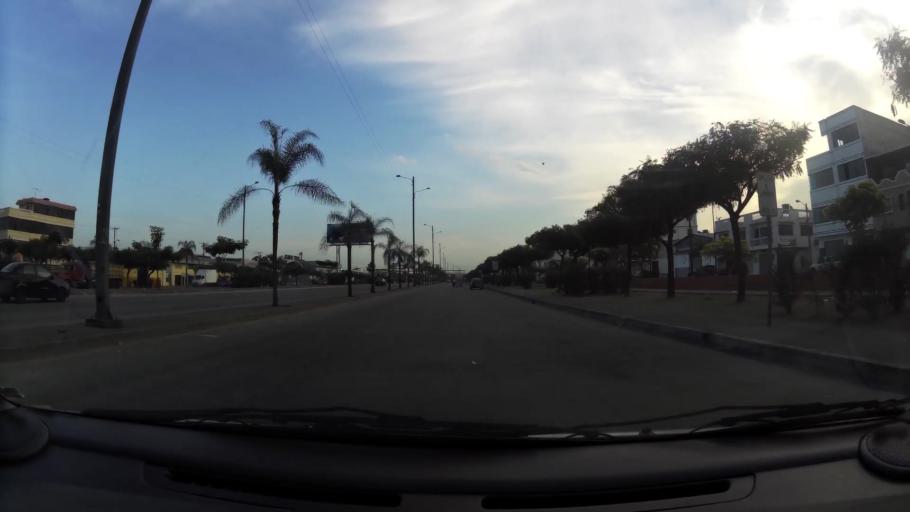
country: EC
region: Guayas
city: Eloy Alfaro
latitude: -2.1354
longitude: -79.8817
